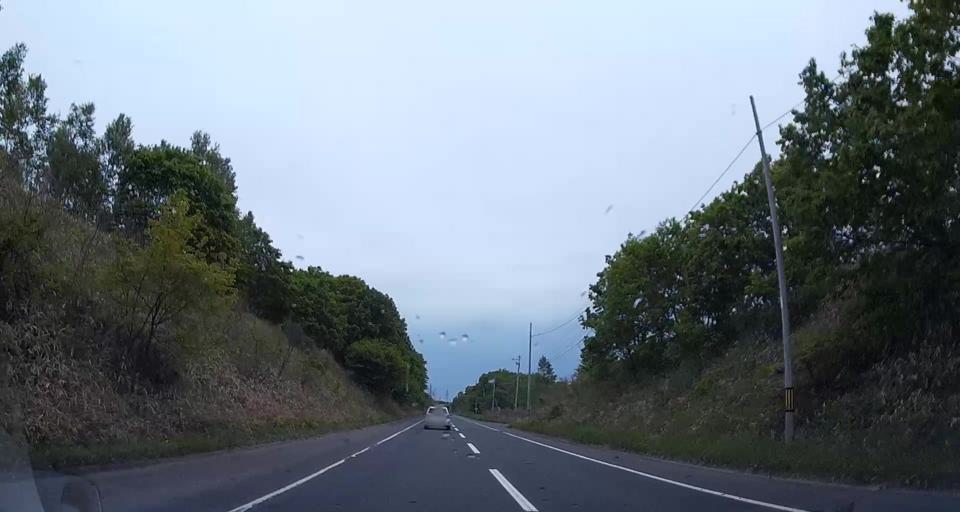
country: JP
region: Hokkaido
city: Chitose
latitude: 42.7042
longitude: 141.7434
